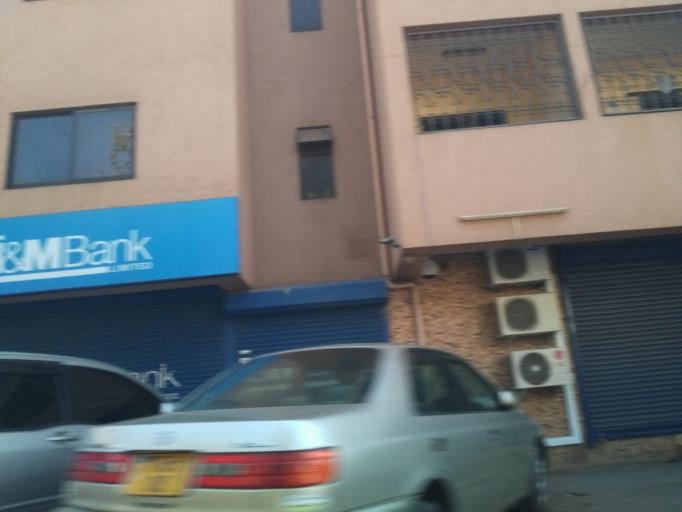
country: TZ
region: Arusha
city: Arusha
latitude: -3.3749
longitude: 36.6887
